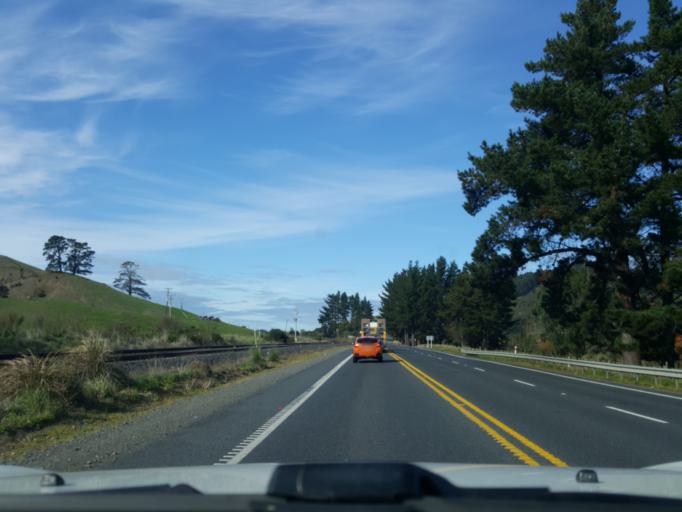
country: NZ
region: Waikato
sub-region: Waikato District
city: Ngaruawahia
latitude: -37.5965
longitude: 175.1623
